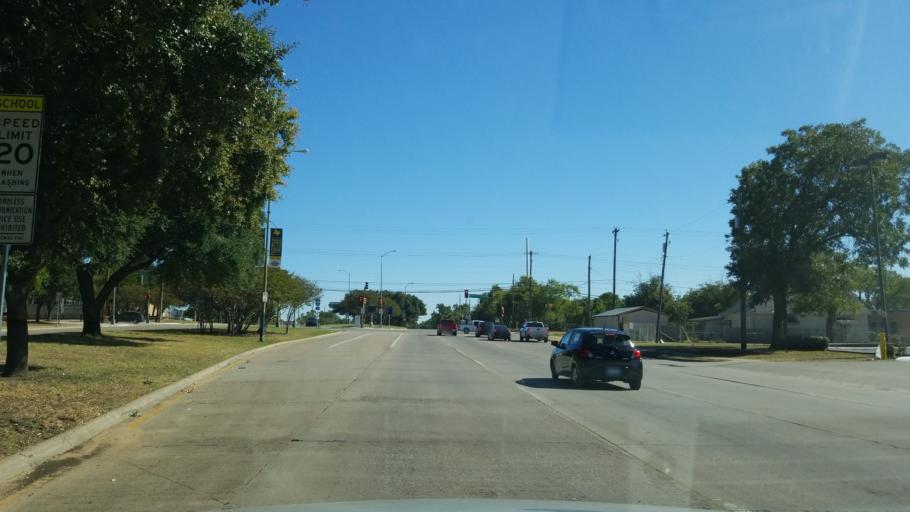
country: US
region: Texas
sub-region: Dallas County
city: Dallas
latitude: 32.7738
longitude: -96.7614
